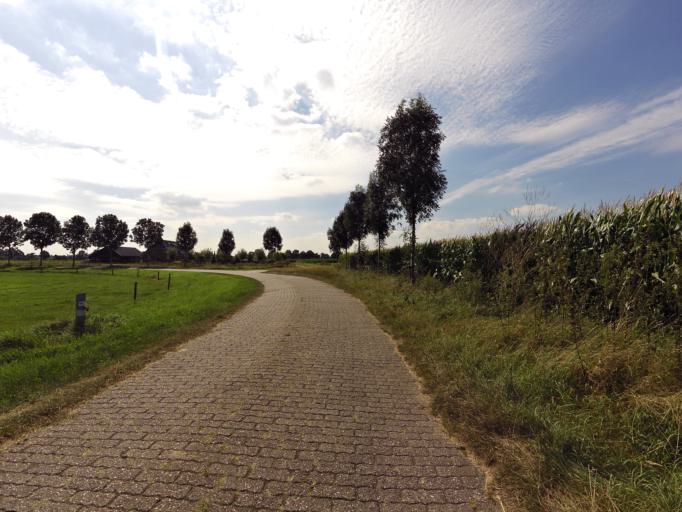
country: NL
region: Gelderland
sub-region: Gemeente Montferland
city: s-Heerenberg
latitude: 51.9315
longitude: 6.1842
